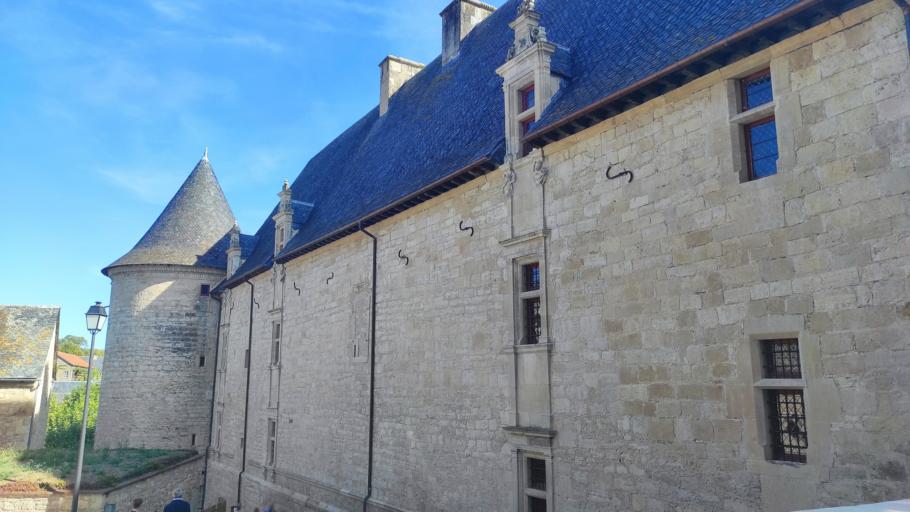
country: FR
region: Midi-Pyrenees
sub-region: Departement de l'Aveyron
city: Cransac
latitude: 44.4599
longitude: 2.2985
